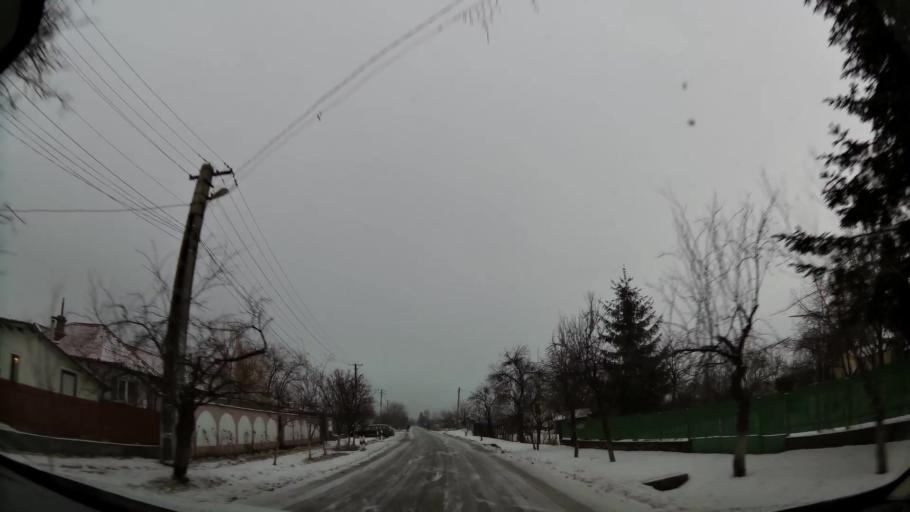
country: RO
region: Prahova
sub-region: Comuna Poenarii-Burchi
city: Ologeni
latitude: 44.7332
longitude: 25.9313
